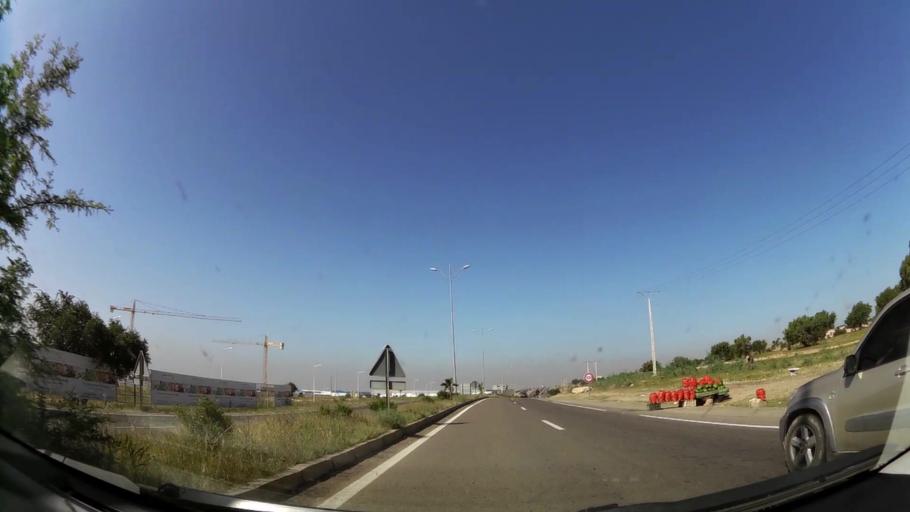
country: MA
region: Souss-Massa-Draa
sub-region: Inezgane-Ait Mellou
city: Inezgane
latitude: 30.4167
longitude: -9.4002
